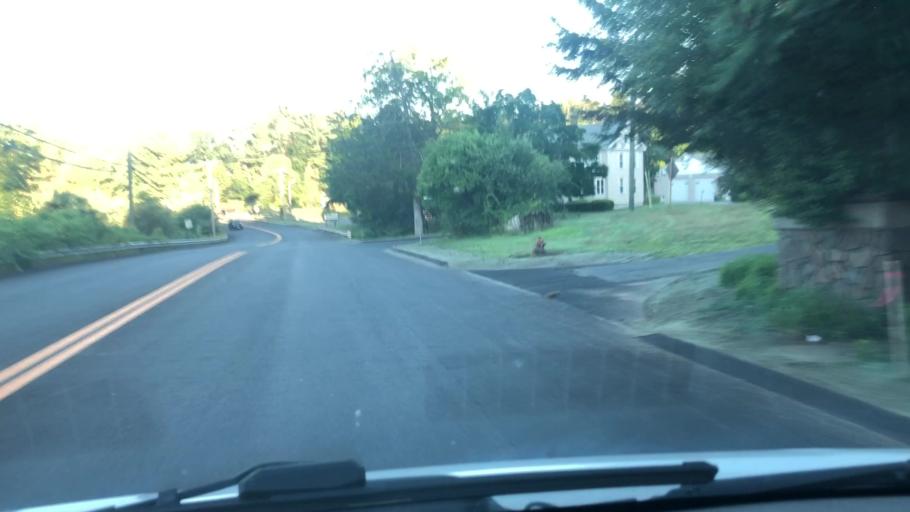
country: US
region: Massachusetts
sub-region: Hampshire County
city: Southampton
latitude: 42.2455
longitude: -72.7101
